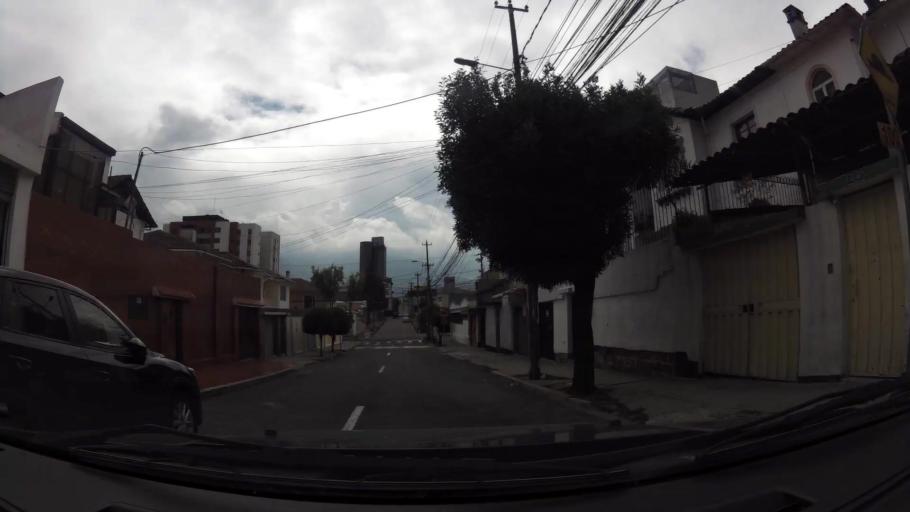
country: EC
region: Pichincha
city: Quito
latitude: -0.2074
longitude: -78.4848
